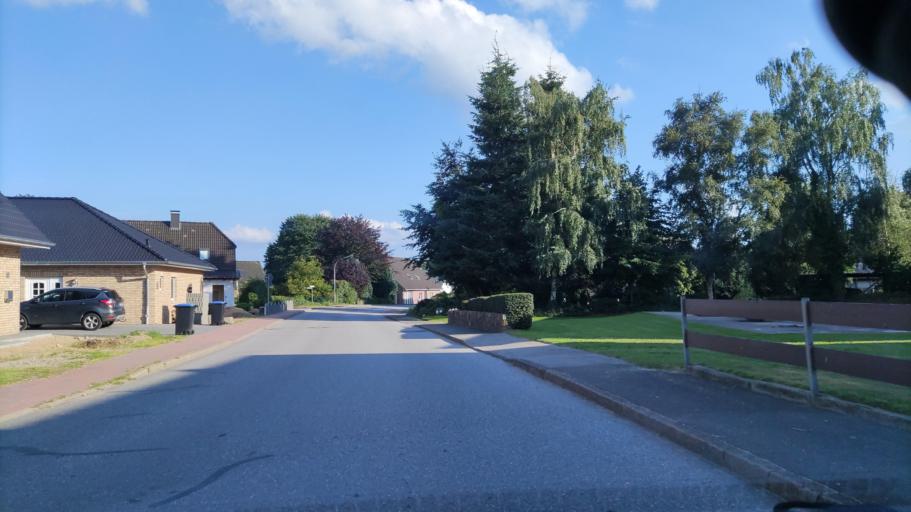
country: DE
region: Schleswig-Holstein
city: Sarlhusen
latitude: 54.0247
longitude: 9.7914
